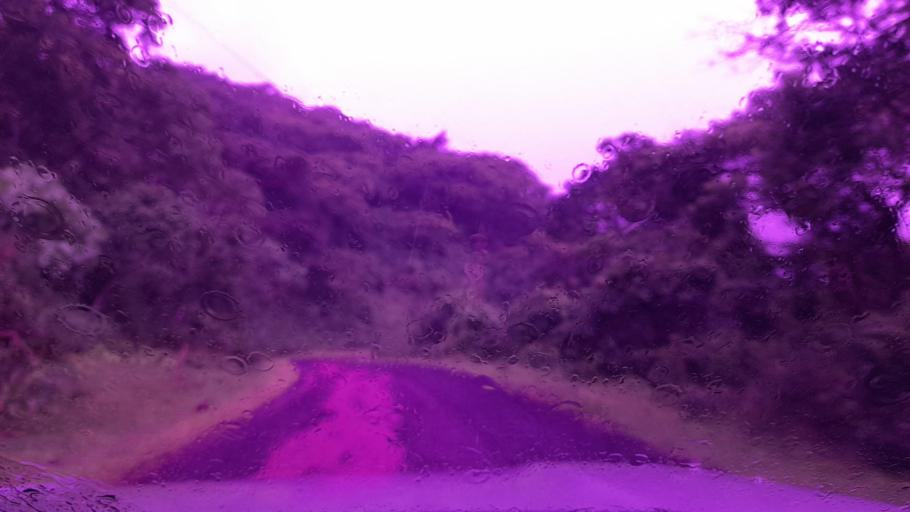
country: ET
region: Oromiya
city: Metu
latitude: 8.4771
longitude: 35.6401
